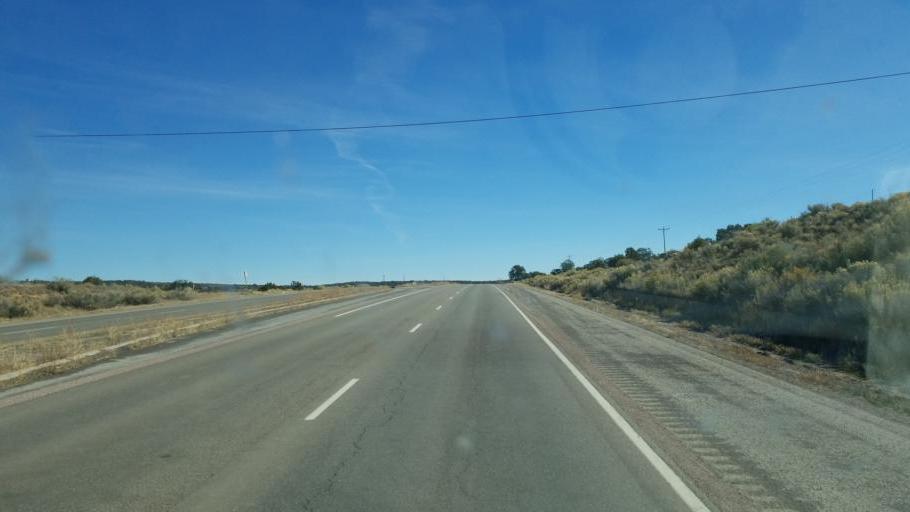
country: US
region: New Mexico
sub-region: McKinley County
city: Twin Lakes
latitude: 35.6322
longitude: -108.9032
